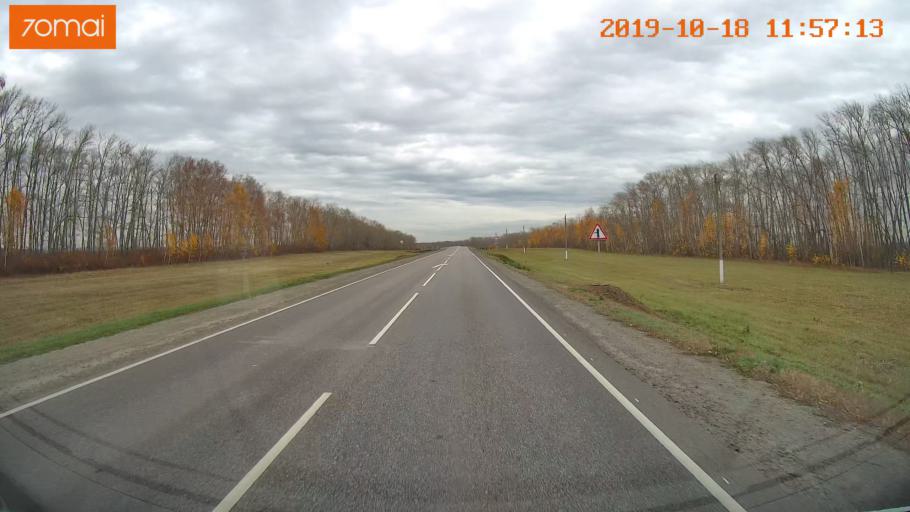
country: RU
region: Rjazan
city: Mikhaylov
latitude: 54.2662
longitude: 39.1377
